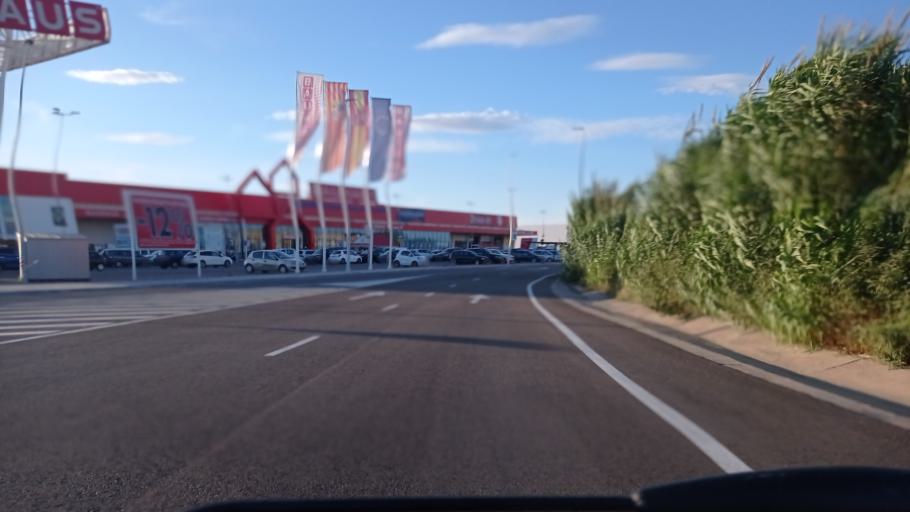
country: ES
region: Aragon
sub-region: Provincia de Zaragoza
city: Oliver-Valdefierro, Oliver, Valdefierro
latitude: 41.6740
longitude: -0.9505
